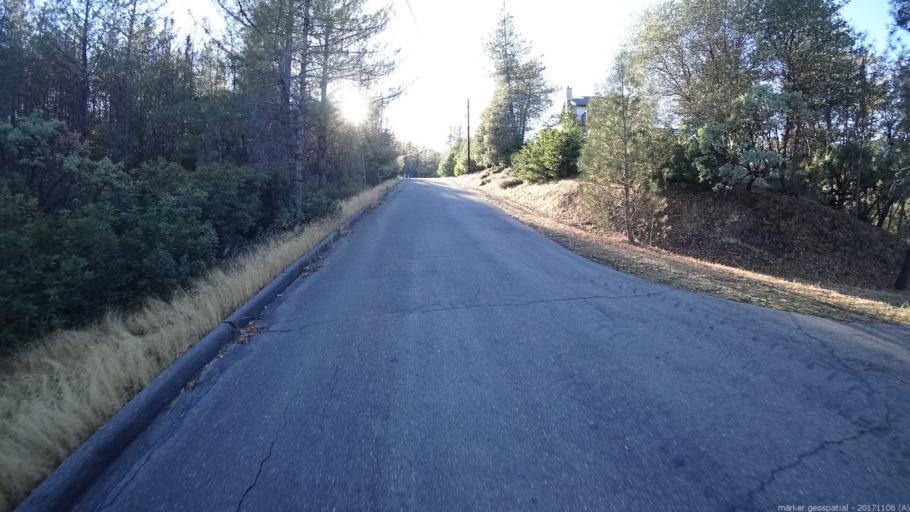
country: US
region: California
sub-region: Shasta County
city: Shasta
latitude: 40.5833
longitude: -122.4930
